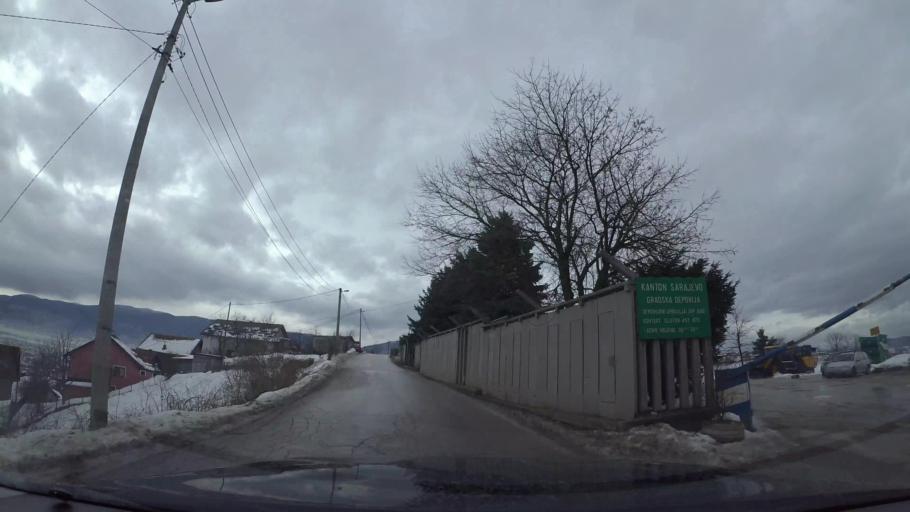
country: BA
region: Federation of Bosnia and Herzegovina
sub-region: Kanton Sarajevo
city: Sarajevo
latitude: 43.8622
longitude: 18.3432
